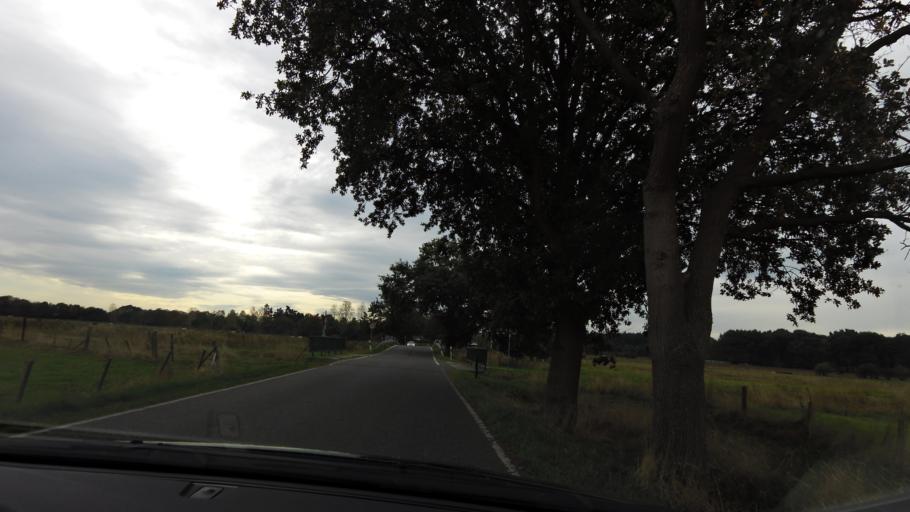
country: DE
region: North Rhine-Westphalia
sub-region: Regierungsbezirk Koln
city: Gangelt
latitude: 50.9850
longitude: 6.0256
